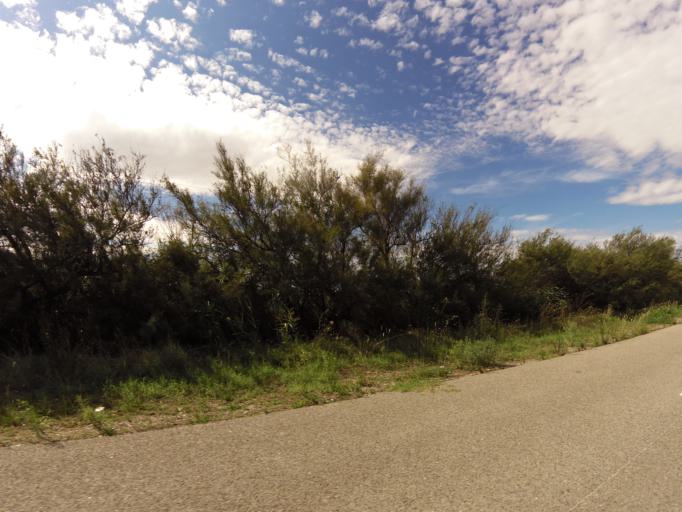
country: FR
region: Languedoc-Roussillon
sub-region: Departement du Gard
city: Aigues-Mortes
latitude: 43.6014
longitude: 4.1944
